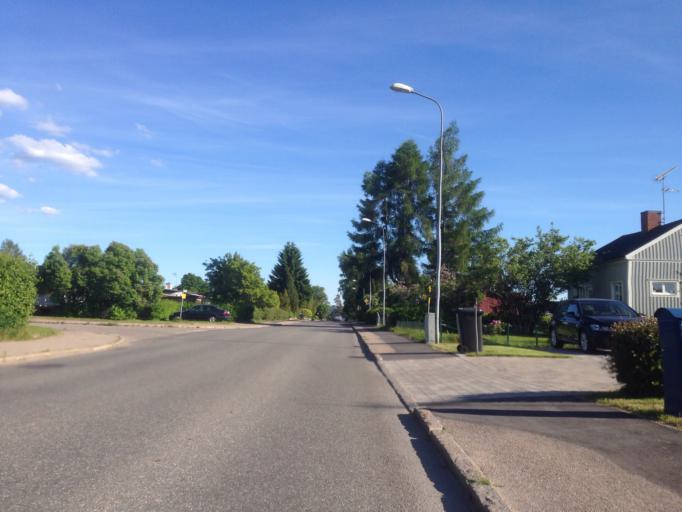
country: SE
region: Dalarna
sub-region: Ludvika Kommun
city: Ludvika
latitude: 60.1234
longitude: 15.1919
